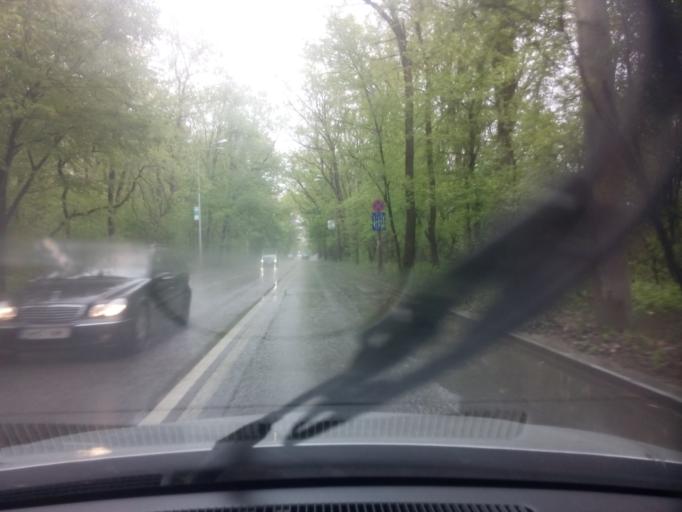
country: RO
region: Ilfov
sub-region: Comuna Otopeni
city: Otopeni
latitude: 44.5159
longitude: 26.0966
